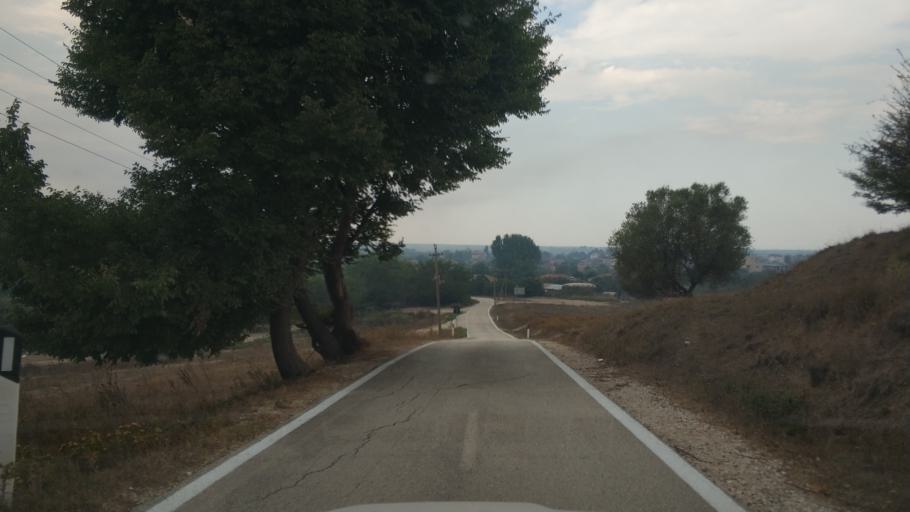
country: AL
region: Fier
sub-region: Rrethi i Fierit
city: Dermenas
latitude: 40.7246
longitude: 19.4689
